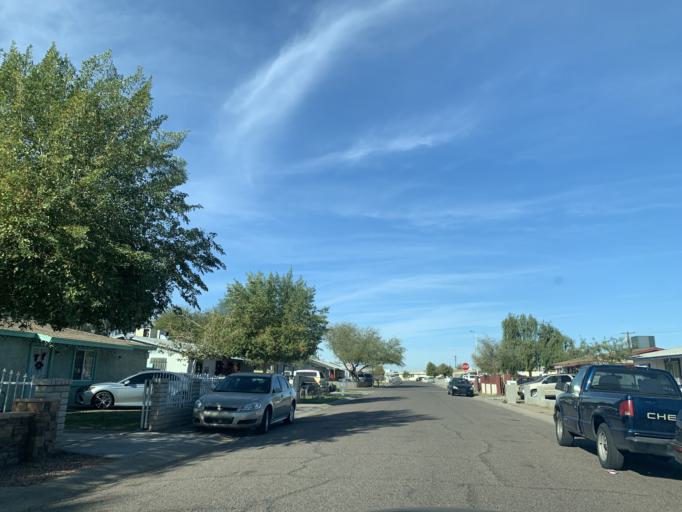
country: US
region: Arizona
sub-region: Maricopa County
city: Laveen
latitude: 33.4041
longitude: -112.1361
